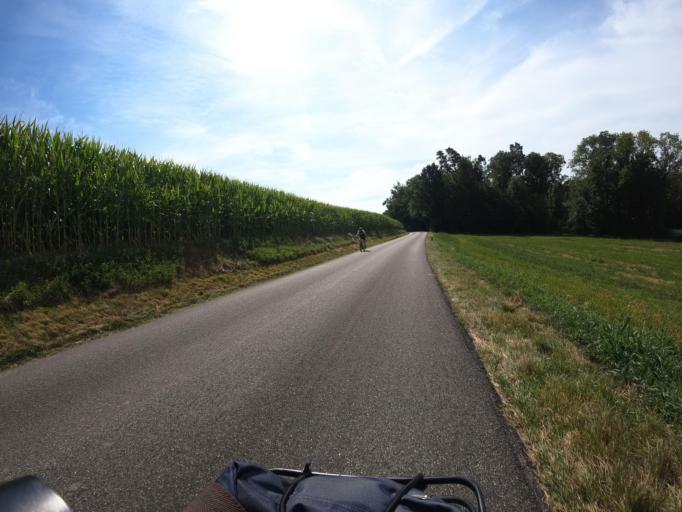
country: CH
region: Zurich
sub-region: Bezirk Affoltern
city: Hedingen
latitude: 47.3085
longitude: 8.4278
